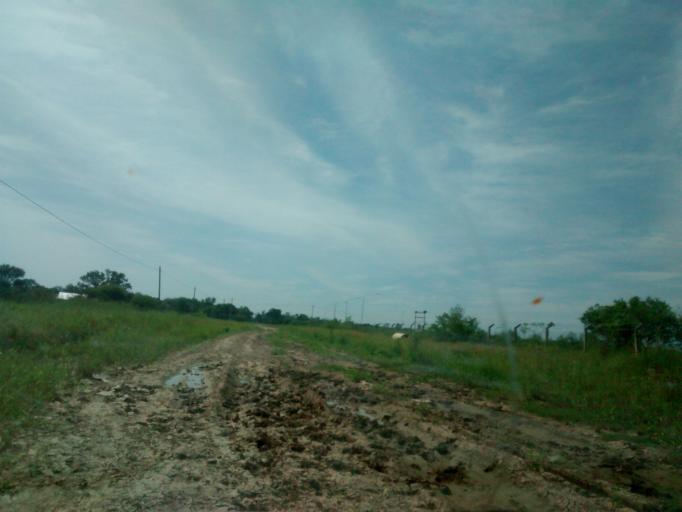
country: AR
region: Chaco
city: Resistencia
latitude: -27.4115
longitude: -58.9595
